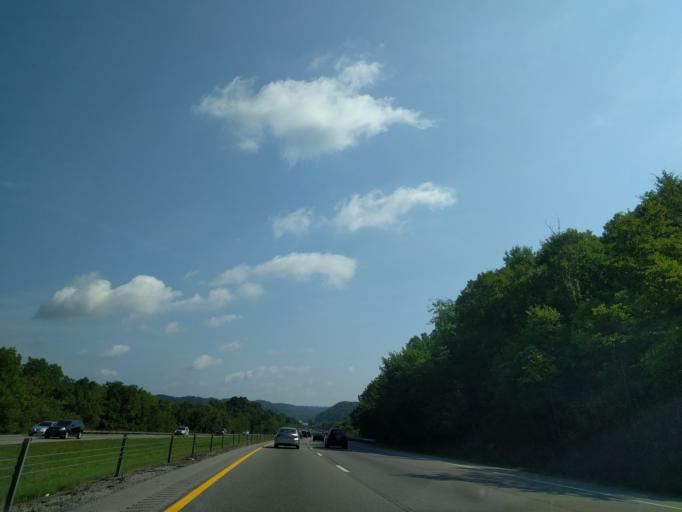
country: US
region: Tennessee
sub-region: Sumner County
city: Millersville
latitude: 36.3619
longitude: -86.7184
